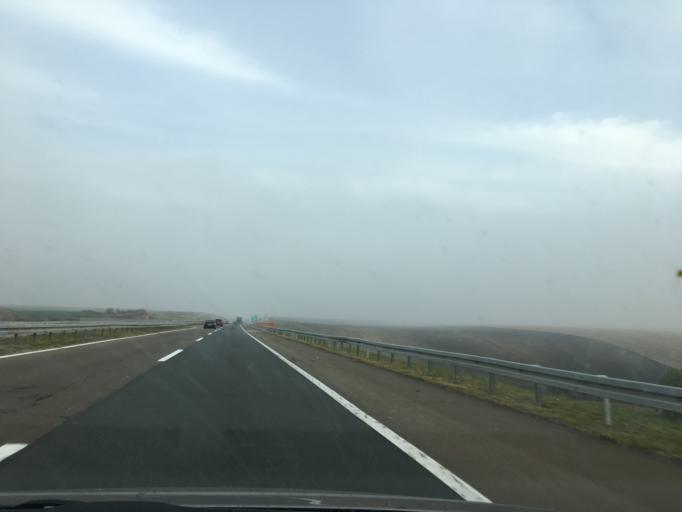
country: RS
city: Beska
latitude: 45.1175
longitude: 20.0981
